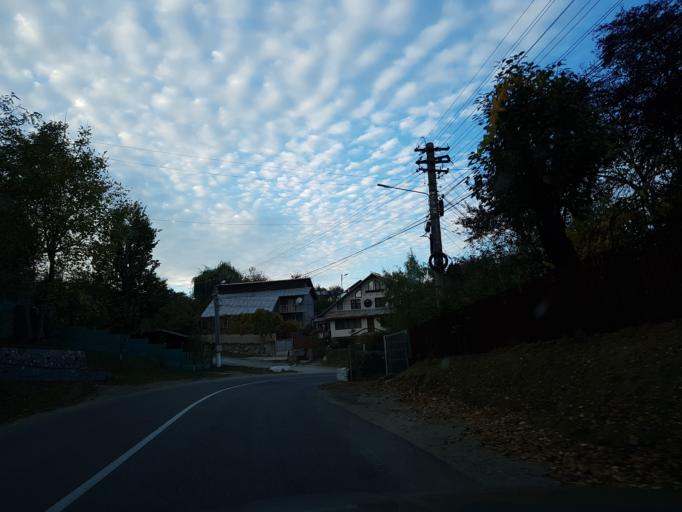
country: RO
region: Prahova
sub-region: Oras Breaza
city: Gura Beliei
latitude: 45.2041
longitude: 25.6491
